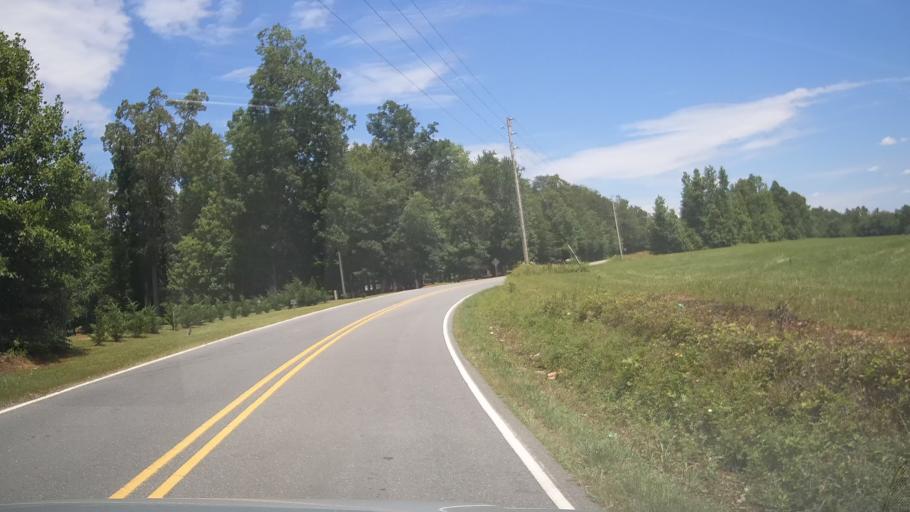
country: US
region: North Carolina
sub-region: Burke County
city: Glen Alpine
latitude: 35.6382
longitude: -81.7949
